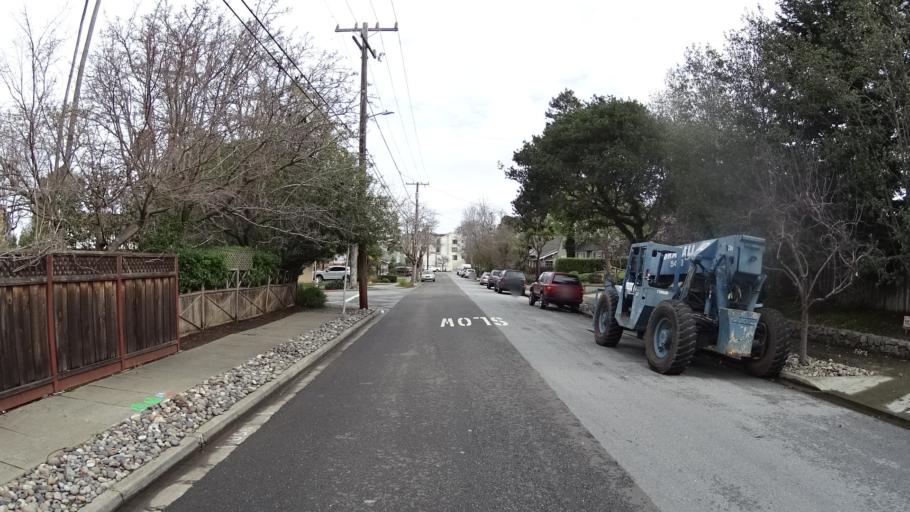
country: US
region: California
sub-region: San Mateo County
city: San Mateo
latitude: 37.5735
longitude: -122.3436
